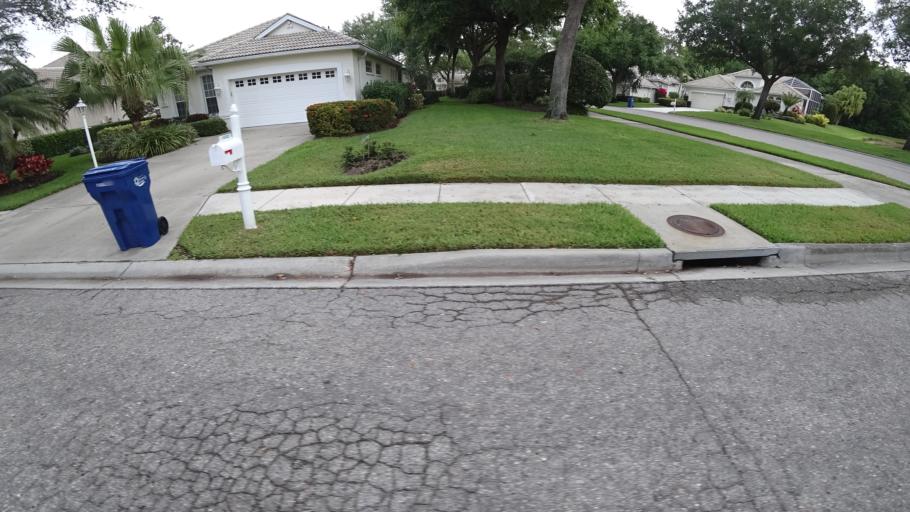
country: US
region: Florida
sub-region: Manatee County
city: Bayshore Gardens
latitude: 27.4374
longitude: -82.6011
